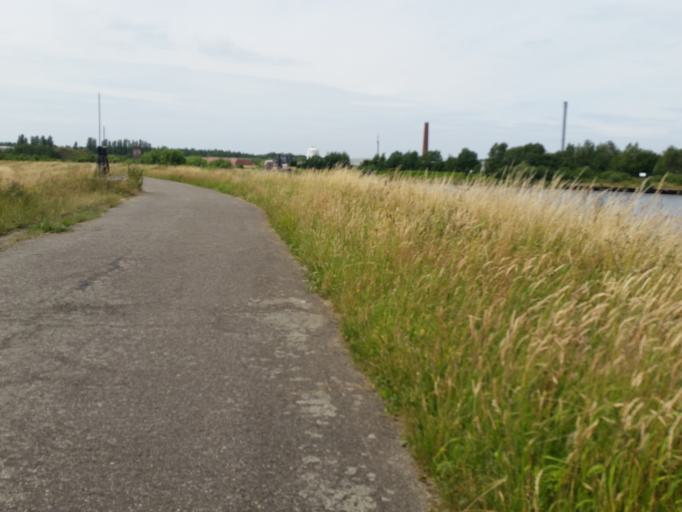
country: BE
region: Flanders
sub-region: Provincie Antwerpen
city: Rumst
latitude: 51.0776
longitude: 4.4152
